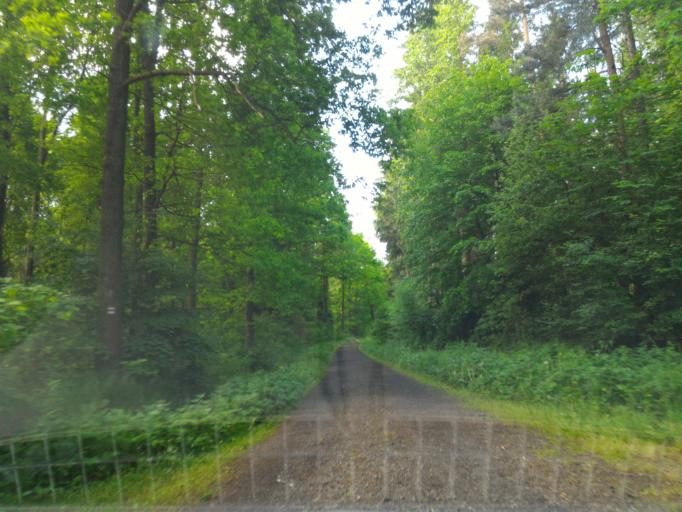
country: DE
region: Saxony
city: Grossschonau
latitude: 50.8784
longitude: 14.6667
